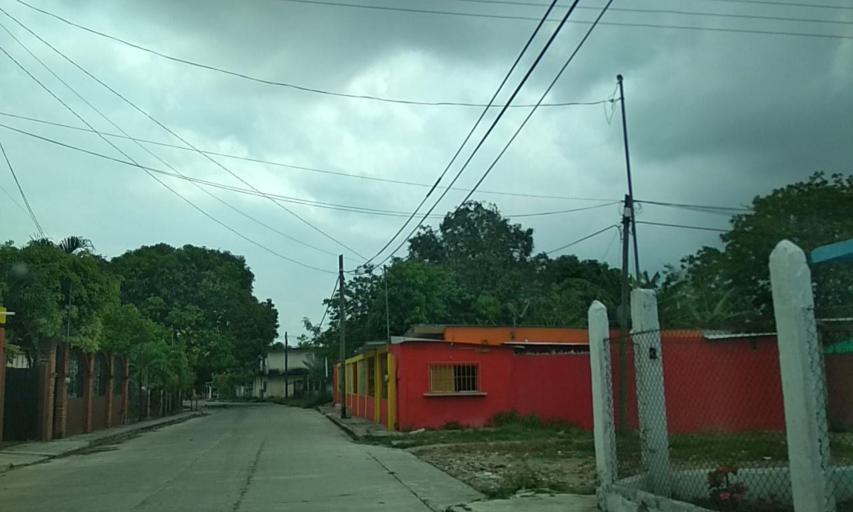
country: MX
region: Veracruz
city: Las Choapas
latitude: 17.8954
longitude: -94.1001
